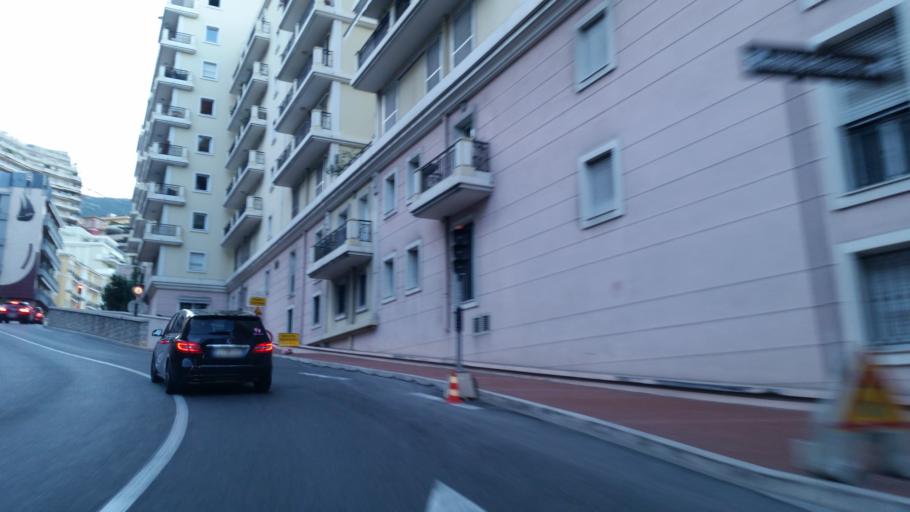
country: MC
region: Commune de Monaco
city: Monaco
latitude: 43.7336
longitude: 7.4177
